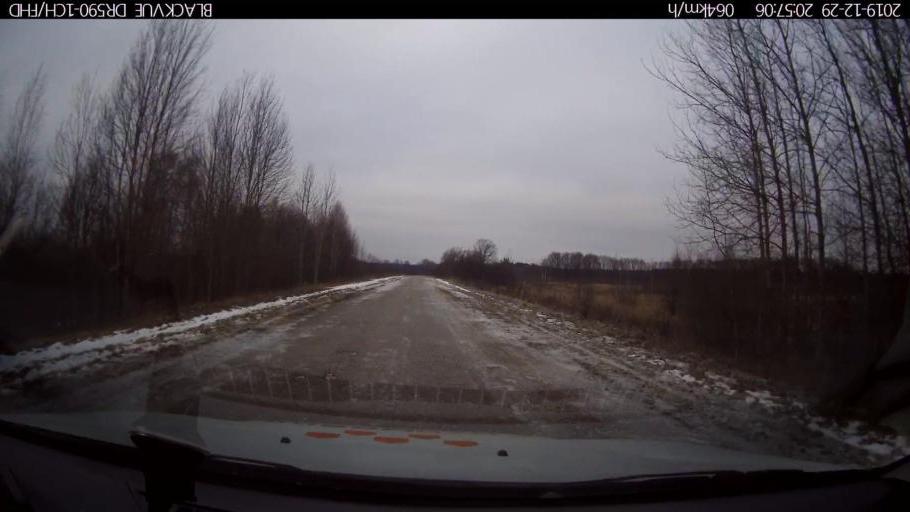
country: RU
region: Nizjnij Novgorod
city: Afonino
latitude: 56.1580
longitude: 43.9942
